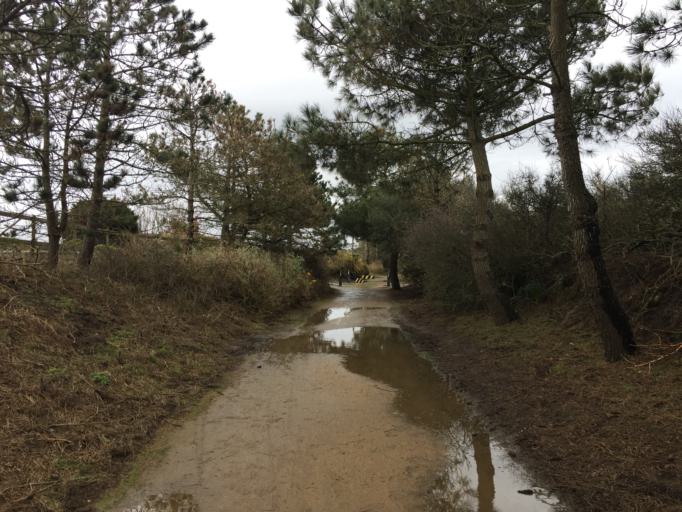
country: JE
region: St Helier
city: Saint Helier
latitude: 49.1820
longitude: -2.2363
